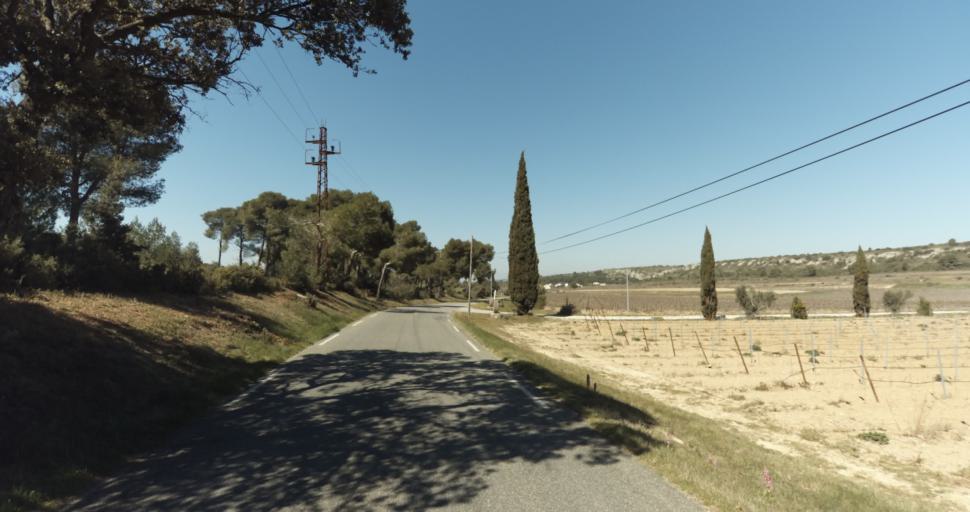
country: FR
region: Provence-Alpes-Cote d'Azur
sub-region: Departement des Bouches-du-Rhone
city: La Fare-les-Oliviers
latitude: 43.6023
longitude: 5.1928
